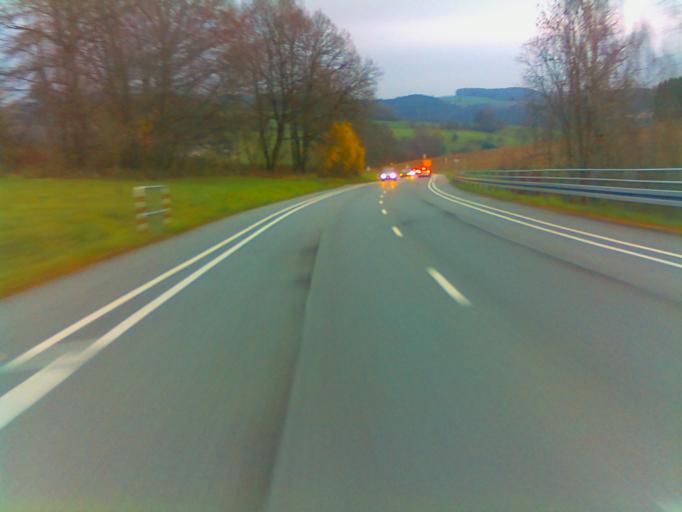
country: DE
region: Hesse
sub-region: Regierungsbezirk Darmstadt
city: Wald-Michelbach
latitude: 49.5579
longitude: 8.8119
